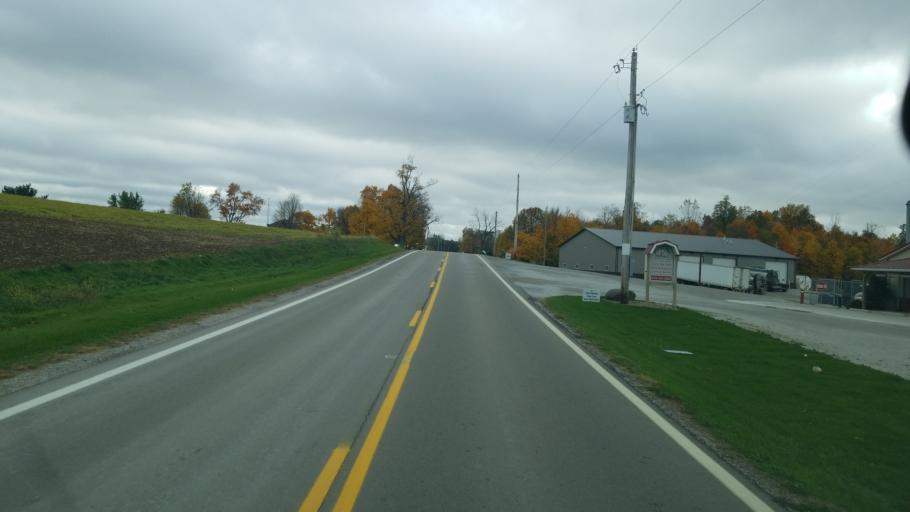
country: US
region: Ohio
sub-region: Richland County
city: Shelby
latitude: 40.9246
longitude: -82.7309
